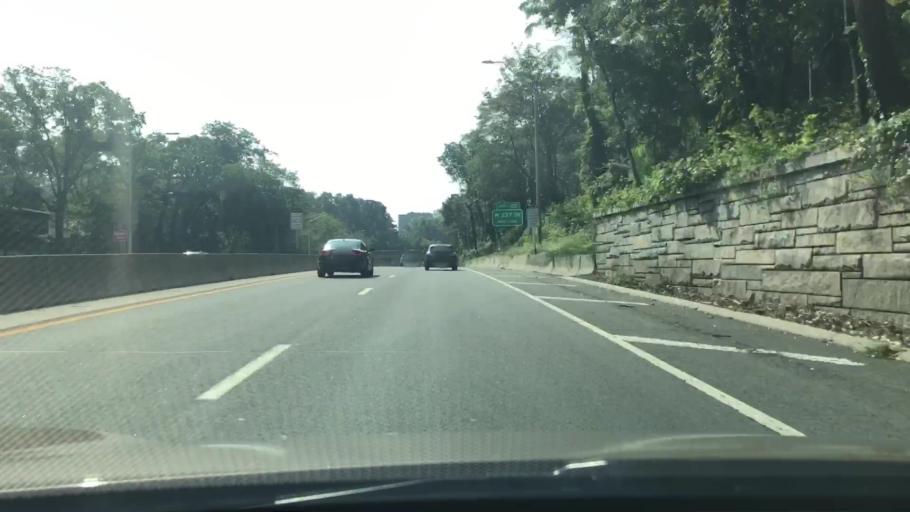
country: US
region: New York
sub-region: New York County
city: Inwood
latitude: 40.8927
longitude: -73.9083
